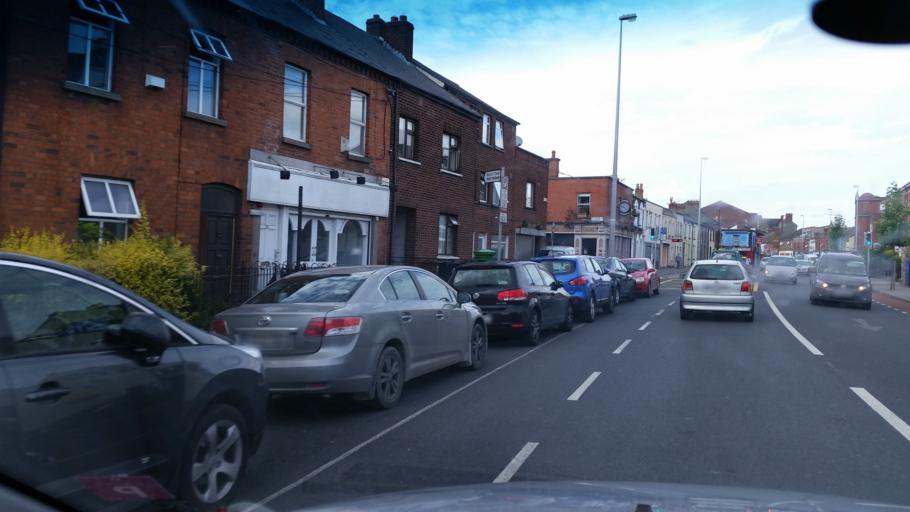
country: IE
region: Leinster
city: Cabra
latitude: 53.3583
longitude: -6.2734
